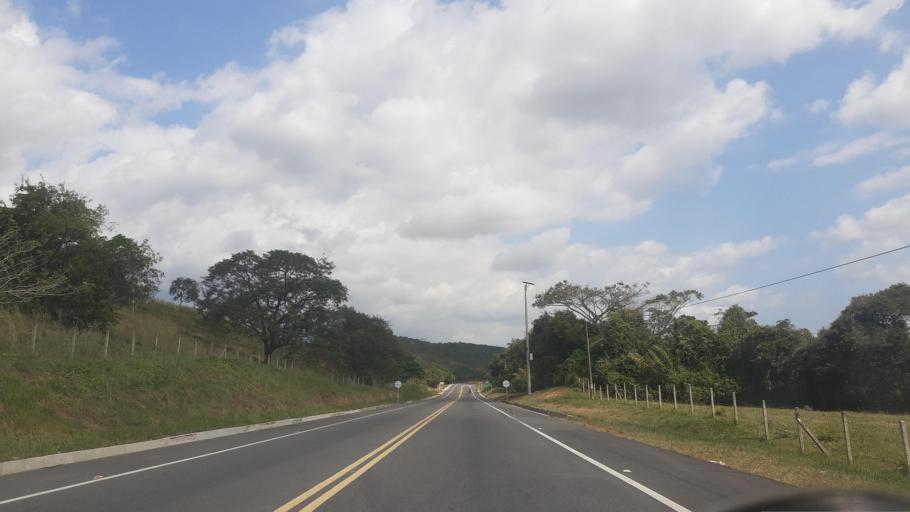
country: CO
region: Casanare
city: Tauramena
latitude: 4.8543
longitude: -72.7193
